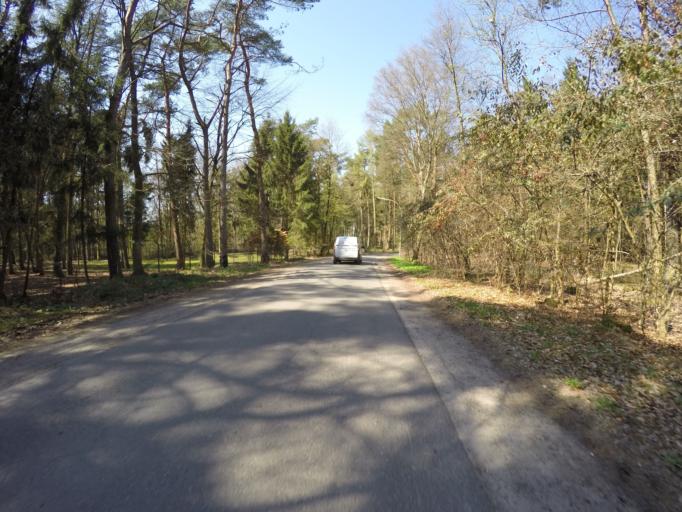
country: DE
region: Schleswig-Holstein
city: Ellerau
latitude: 53.7363
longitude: 9.9360
